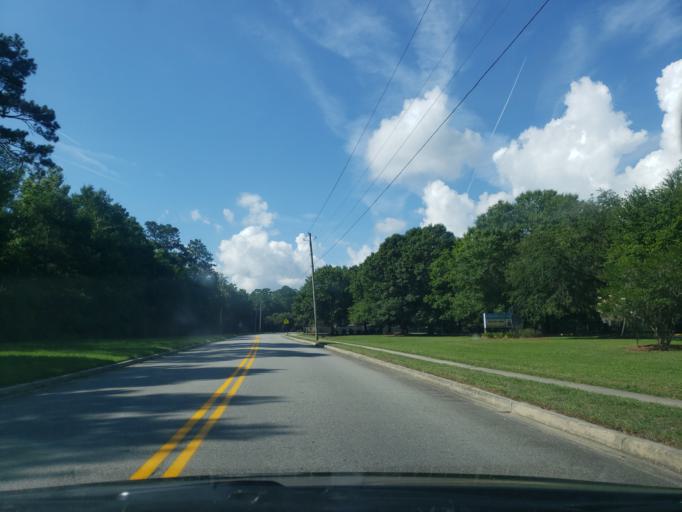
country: US
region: Georgia
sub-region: Chatham County
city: Georgetown
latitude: 31.9761
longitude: -81.2274
